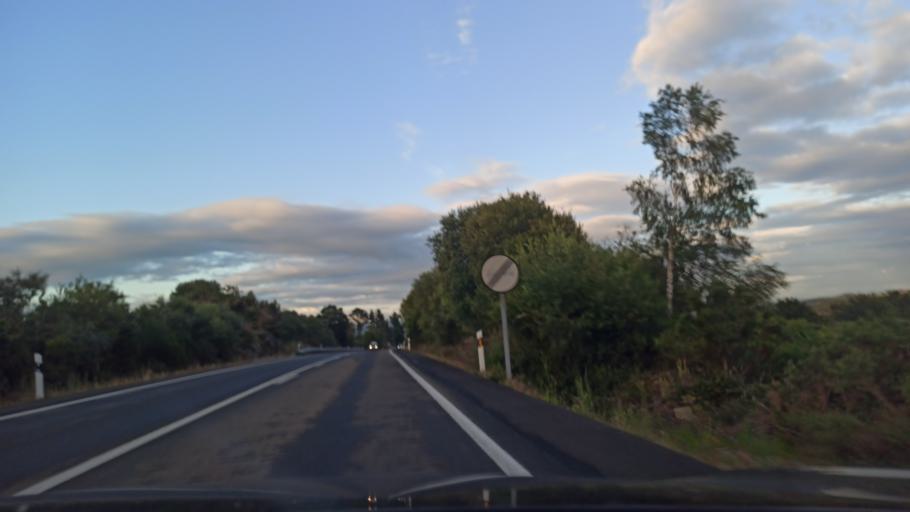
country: ES
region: Galicia
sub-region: Provincia de Pontevedra
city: Rodeiro
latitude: 42.7726
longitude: -7.9608
